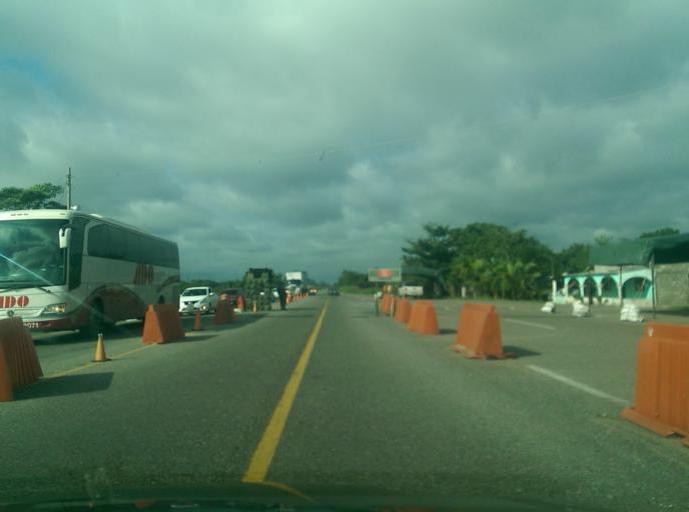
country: MX
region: Tabasco
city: Aquiles Serdan
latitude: 17.6932
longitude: -92.3153
